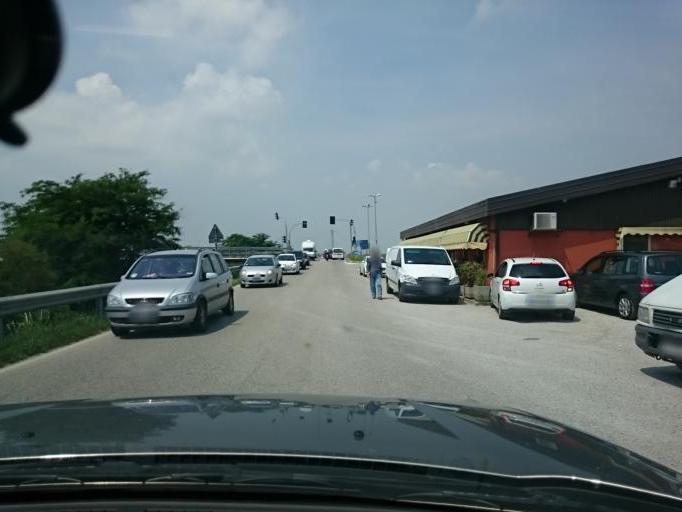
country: IT
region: Veneto
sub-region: Provincia di Padova
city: Codevigo
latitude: 45.2460
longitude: 12.1275
